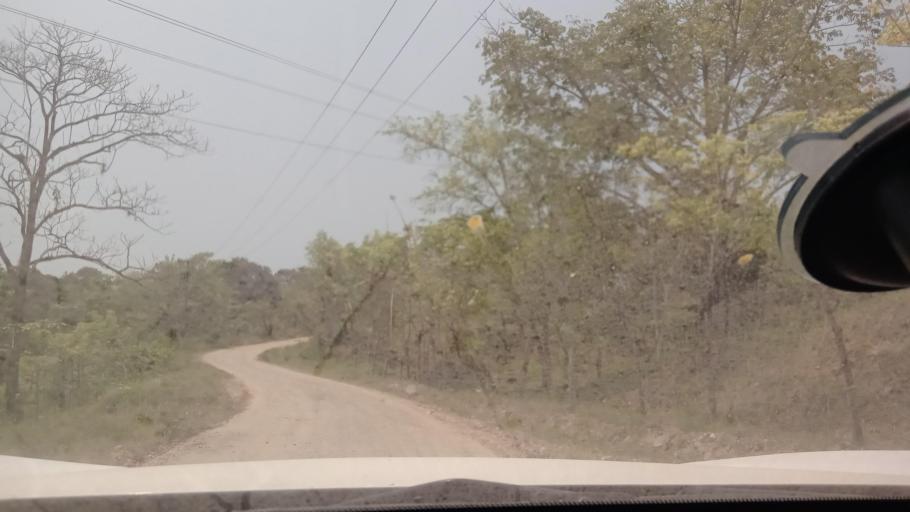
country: MX
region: Chiapas
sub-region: Tecpatan
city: Raudales Malpaso
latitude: 17.4492
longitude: -93.7906
